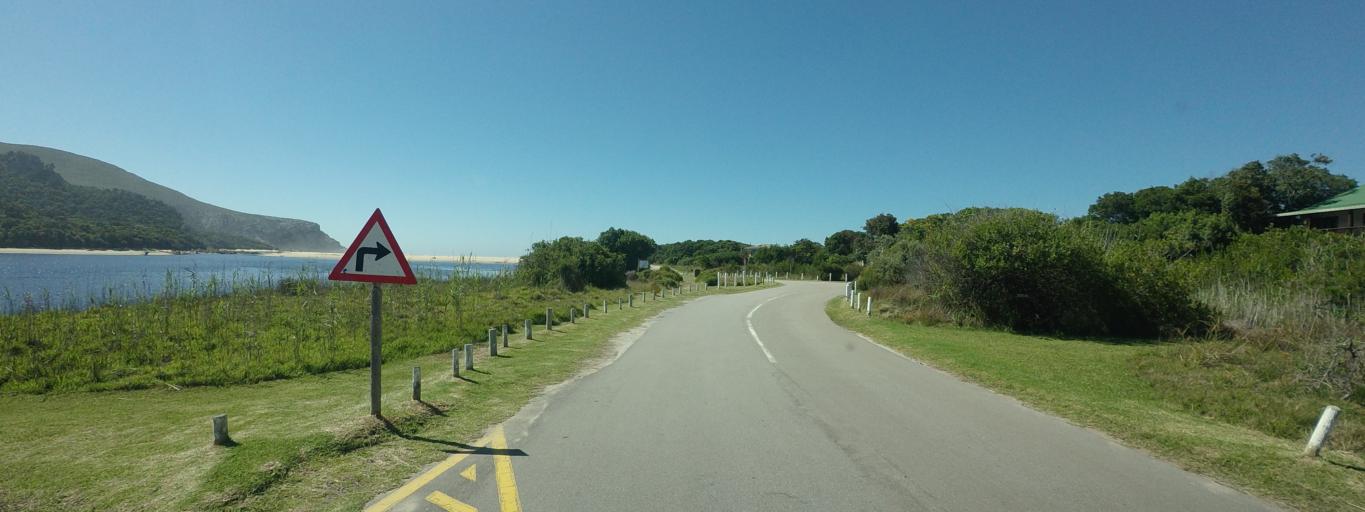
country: ZA
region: Western Cape
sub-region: Eden District Municipality
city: Plettenberg Bay
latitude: -33.9784
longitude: 23.5641
